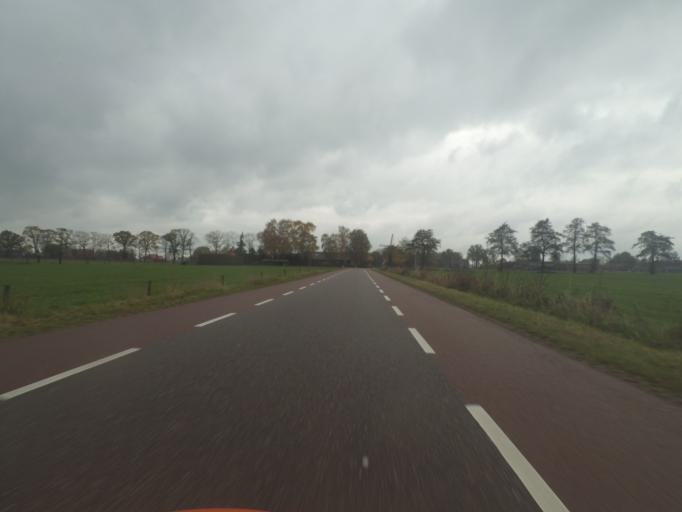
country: NL
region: Gelderland
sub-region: Gemeente Barneveld
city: Barneveld
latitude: 52.1108
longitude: 5.5554
